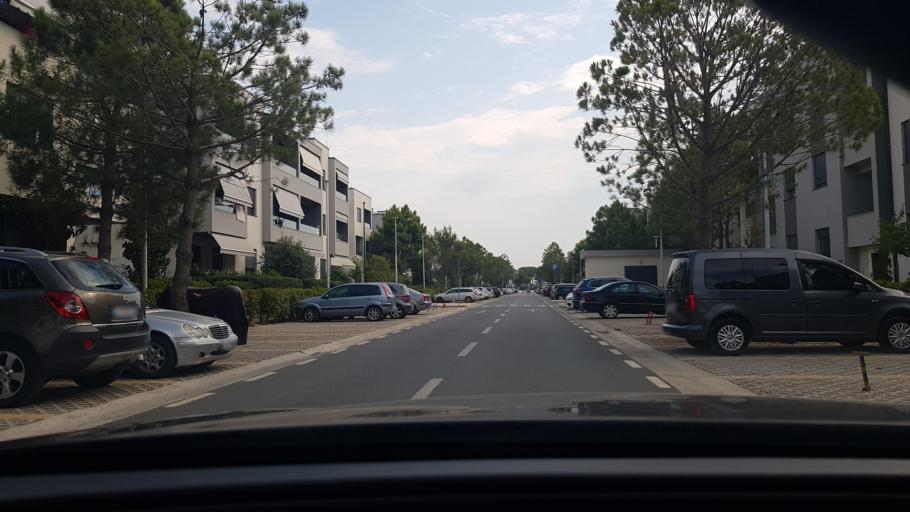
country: AL
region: Durres
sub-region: Rrethi i Durresit
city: Katundi i Ri
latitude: 41.4914
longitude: 19.5135
